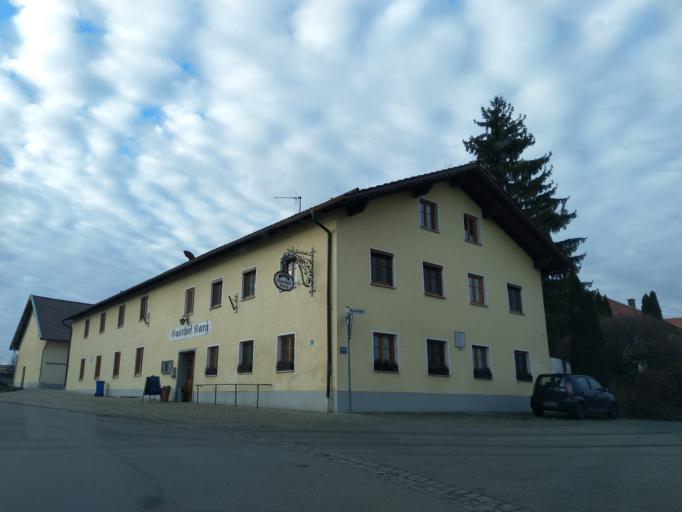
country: DE
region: Bavaria
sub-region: Lower Bavaria
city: Aholming
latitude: 48.7349
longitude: 12.9102
